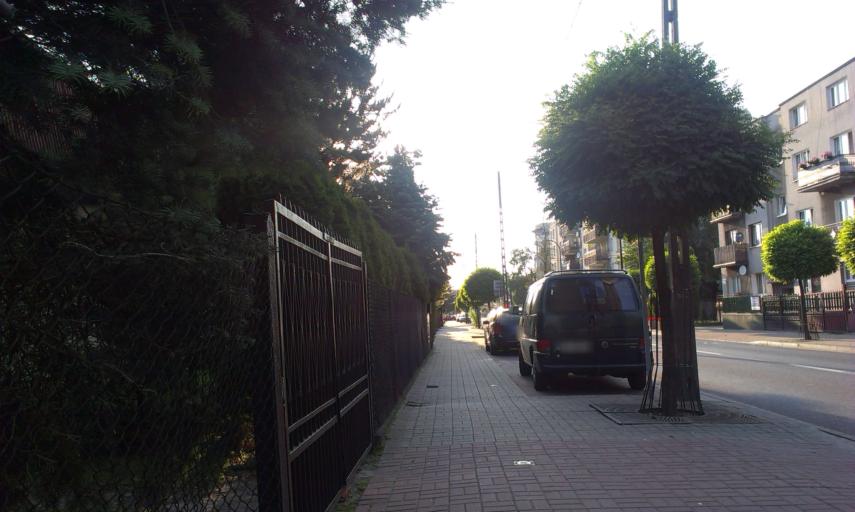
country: PL
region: Masovian Voivodeship
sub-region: Warszawa
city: Ursus
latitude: 52.1946
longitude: 20.8882
